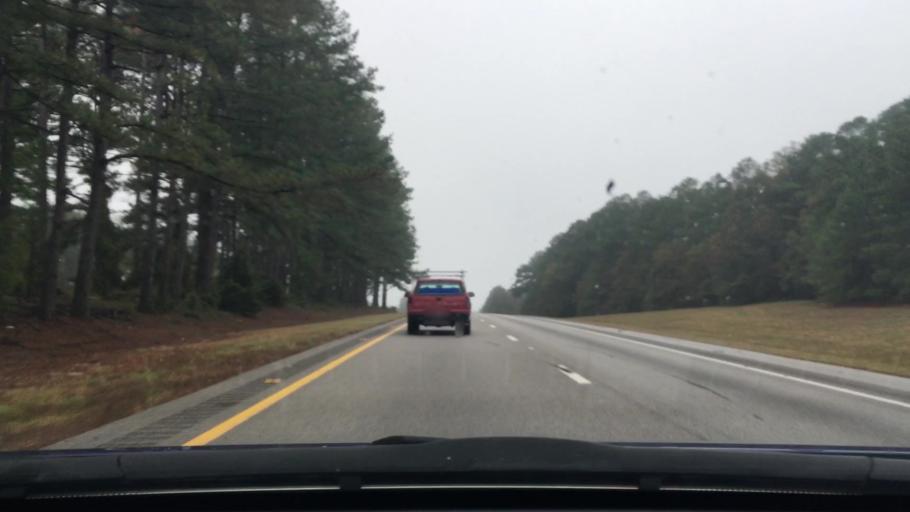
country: US
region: South Carolina
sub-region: Kershaw County
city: Camden
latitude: 34.2089
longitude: -80.4632
